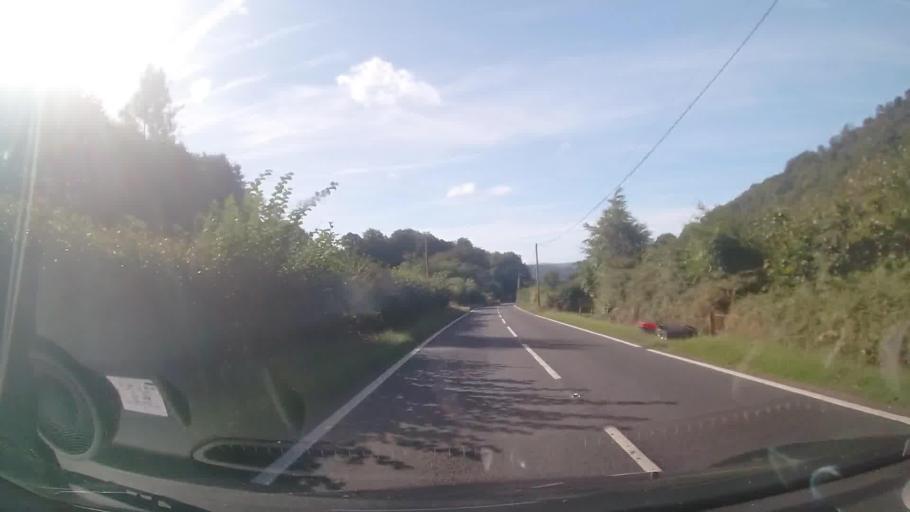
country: GB
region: Wales
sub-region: Blaenau Gwent
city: Brynmawr
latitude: 51.9145
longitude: -3.1911
